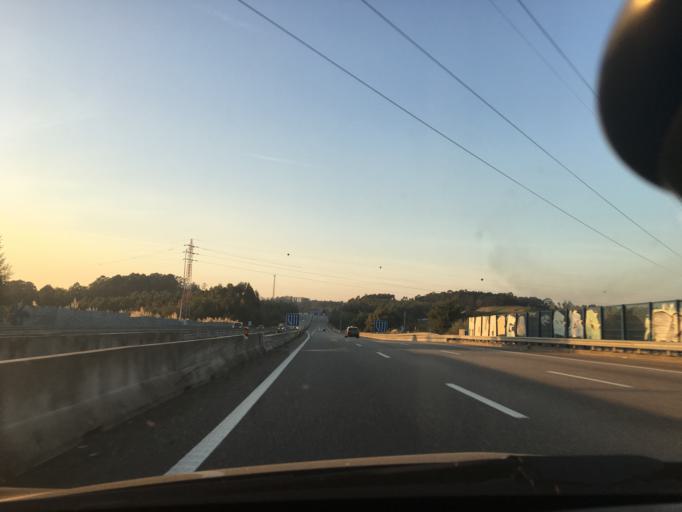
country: PT
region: Porto
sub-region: Matosinhos
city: Guifoes
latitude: 41.2153
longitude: -8.6546
